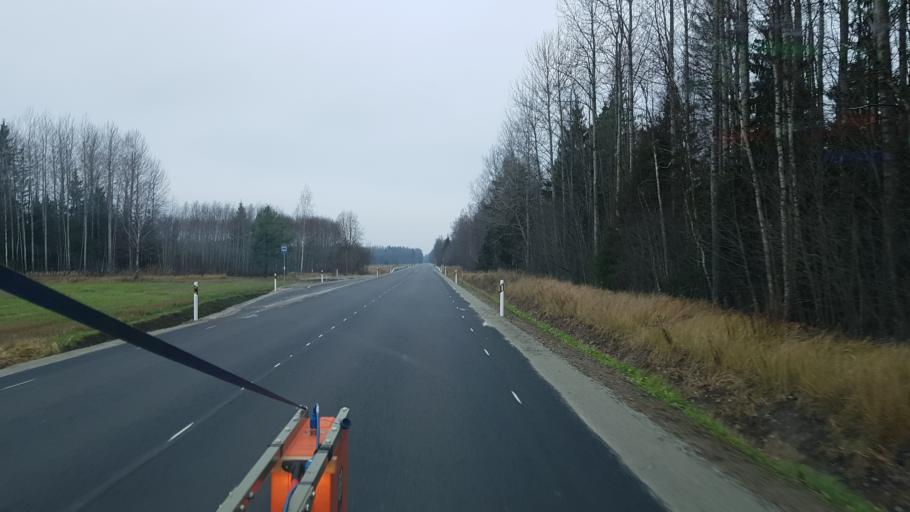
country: EE
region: Paernumaa
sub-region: Vaendra vald (alev)
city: Vandra
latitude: 58.8382
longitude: 25.0747
